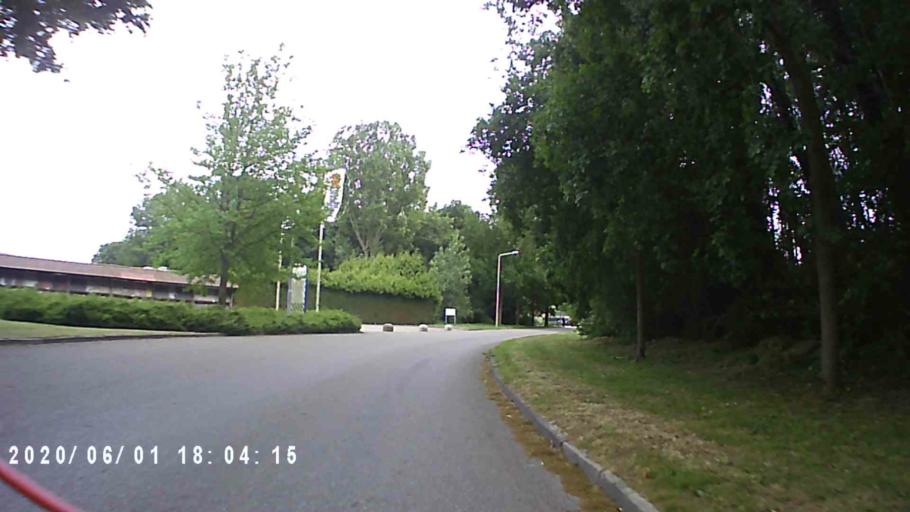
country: NL
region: Friesland
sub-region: Gemeente Tytsjerksteradiel
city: Sumar
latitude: 53.1832
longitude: 5.9931
